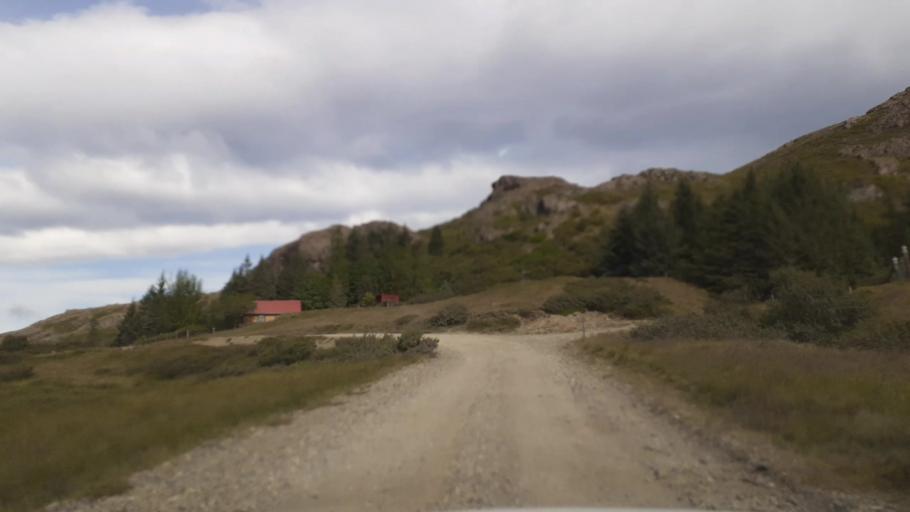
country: IS
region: East
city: Hoefn
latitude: 64.4346
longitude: -14.8963
